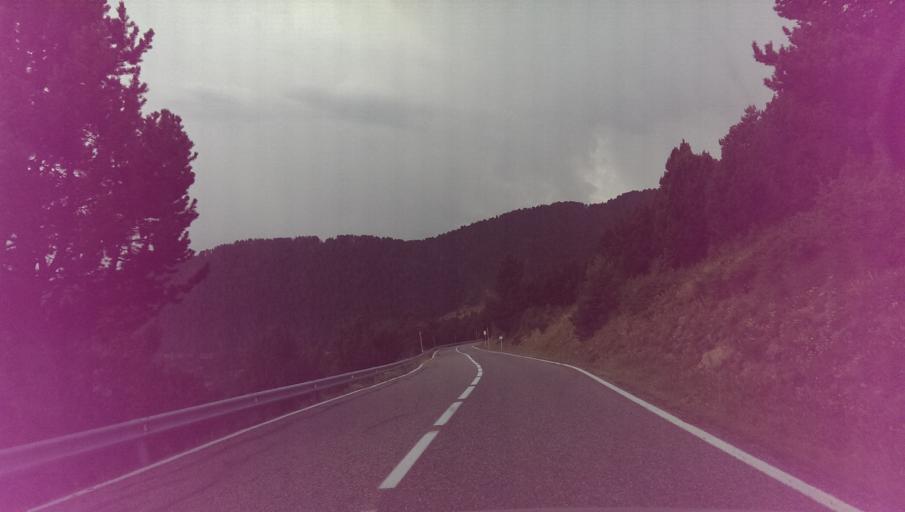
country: AD
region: Canillo
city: Canillo
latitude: 42.5669
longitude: 1.5836
